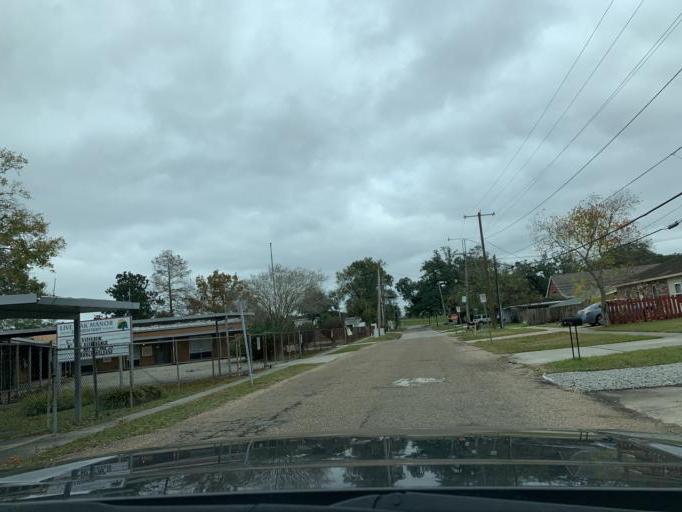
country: US
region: Louisiana
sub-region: Jefferson Parish
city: River Ridge
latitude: 29.9551
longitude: -90.2383
